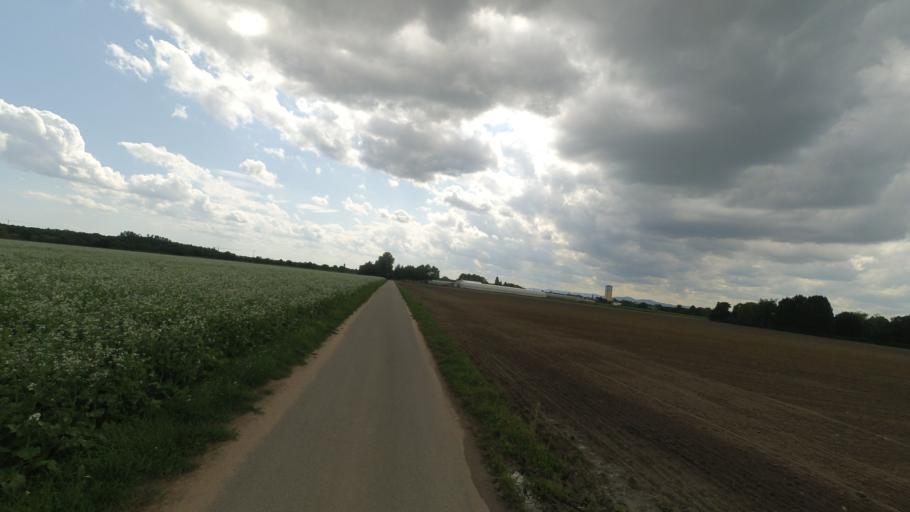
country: DE
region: Rheinland-Pfalz
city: Schifferstadt
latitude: 49.3954
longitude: 8.3999
